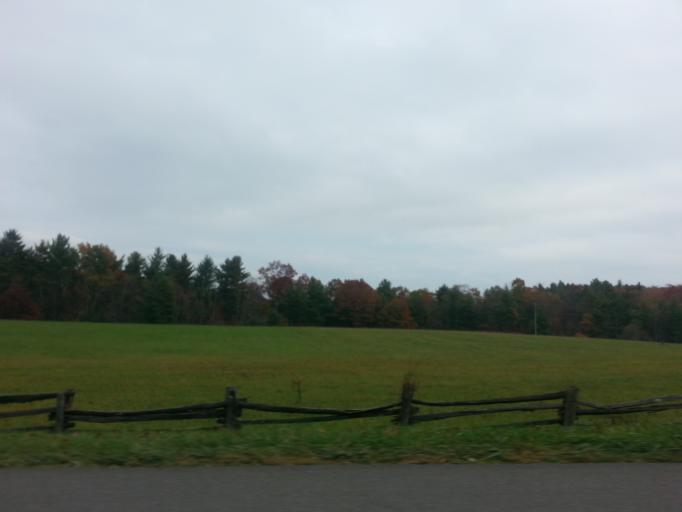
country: US
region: North Carolina
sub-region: Ashe County
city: Jefferson
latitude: 36.3538
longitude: -81.3723
